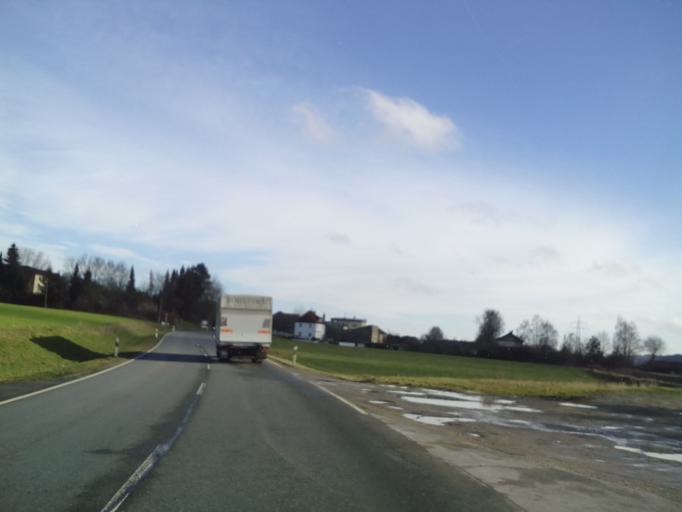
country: DE
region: Bavaria
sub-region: Upper Franconia
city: Altenkunstadt
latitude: 50.1233
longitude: 11.3129
